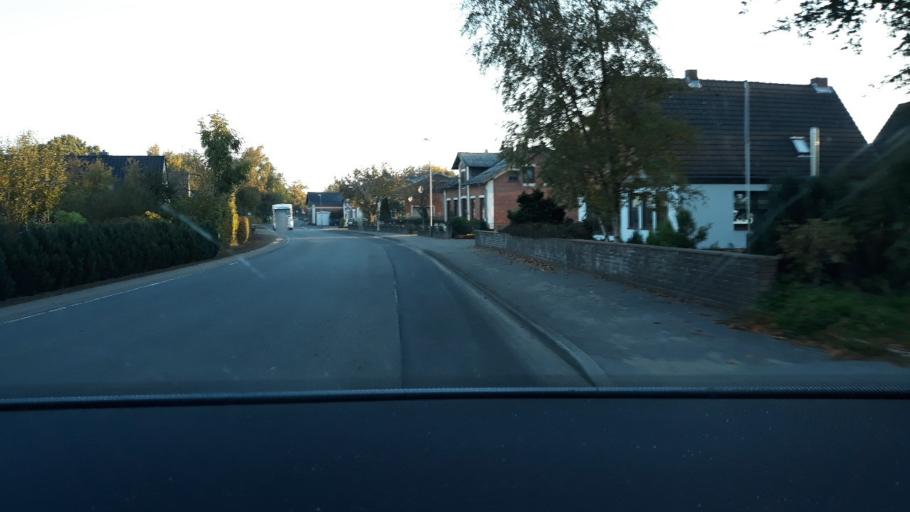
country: DE
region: Schleswig-Holstein
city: Satrup
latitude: 54.6799
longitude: 9.6032
